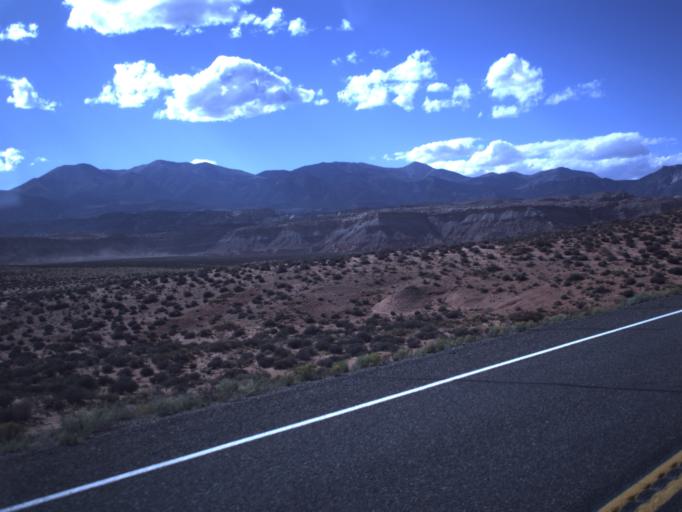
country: US
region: Utah
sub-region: Wayne County
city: Loa
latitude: 38.0674
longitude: -110.6040
